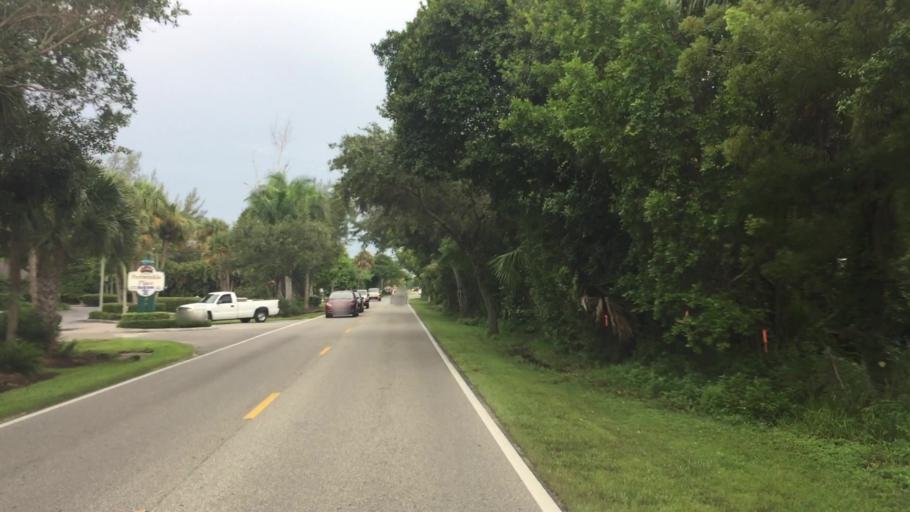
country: US
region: Florida
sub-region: Lee County
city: Sanibel
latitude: 26.4385
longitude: -82.0693
